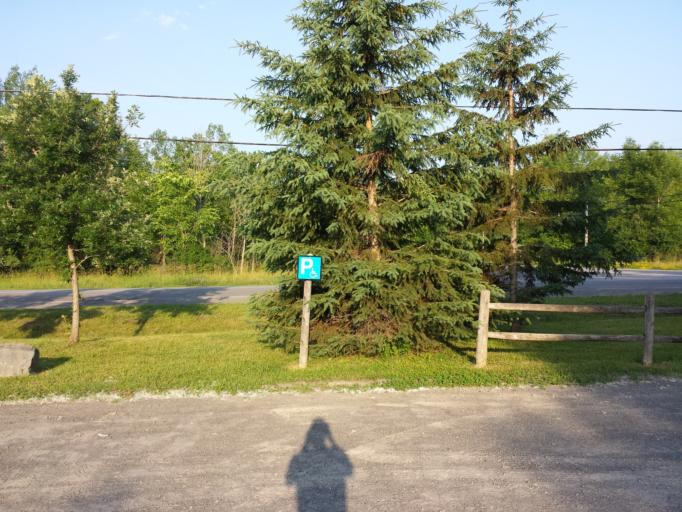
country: CA
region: Ontario
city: Bells Corners
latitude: 45.3645
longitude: -75.8827
